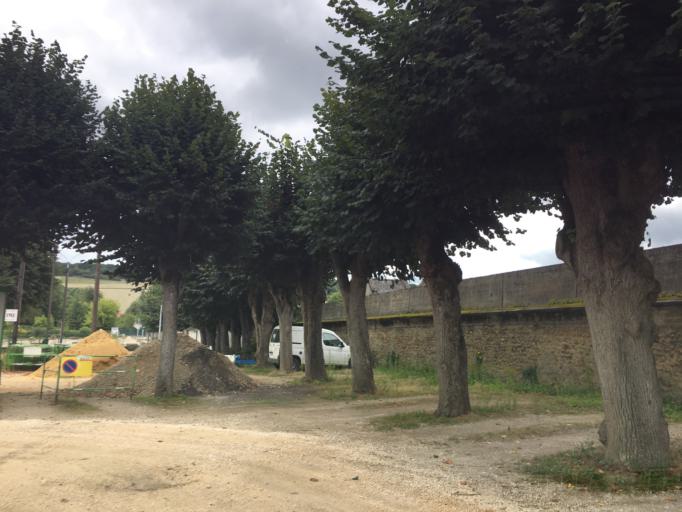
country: FR
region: Bourgogne
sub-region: Departement de l'Yonne
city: Villeneuve-sur-Yonne
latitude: 48.0793
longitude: 3.2940
